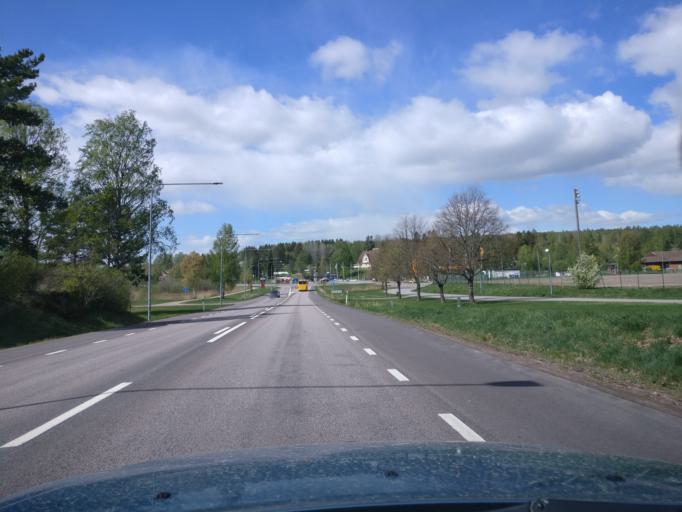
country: SE
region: Vaermland
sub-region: Karlstads Kommun
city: Molkom
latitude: 59.5974
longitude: 13.7245
